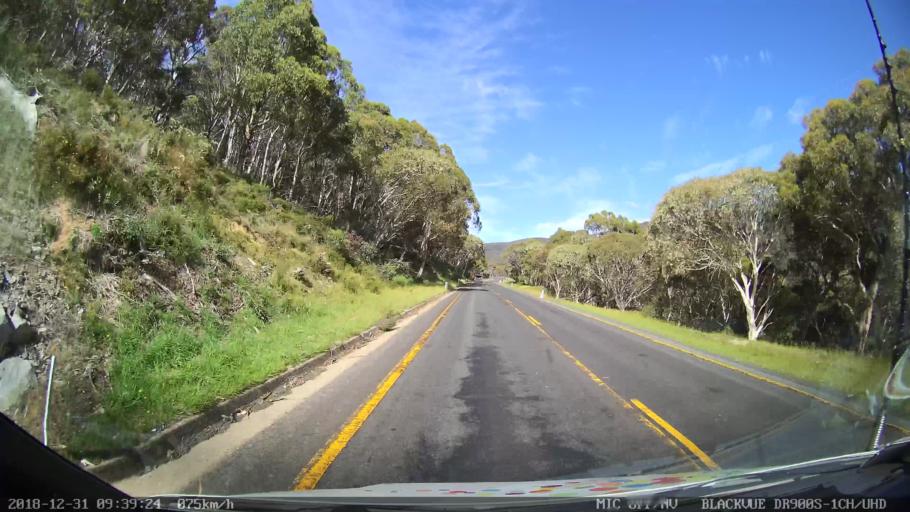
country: AU
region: New South Wales
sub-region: Snowy River
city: Jindabyne
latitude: -36.4790
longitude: 148.3554
